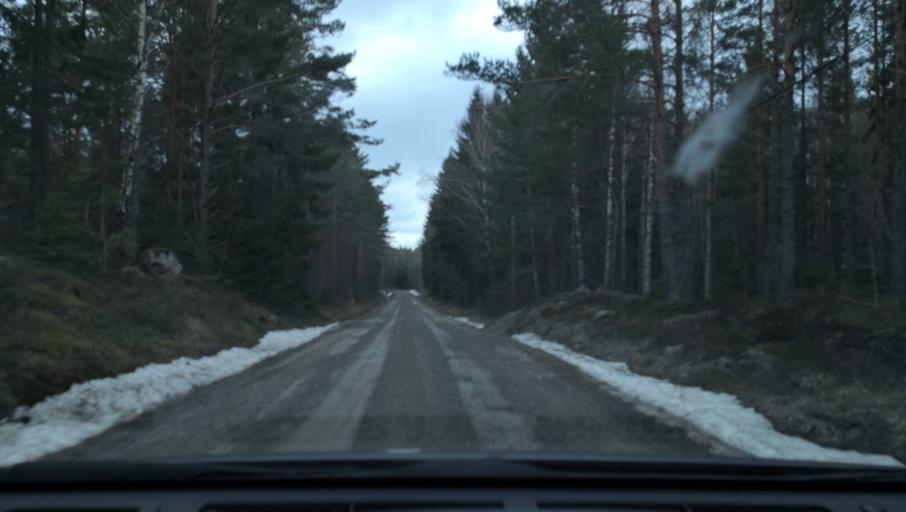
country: SE
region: Vaestmanland
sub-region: Kopings Kommun
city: Kolsva
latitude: 59.6010
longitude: 15.6616
